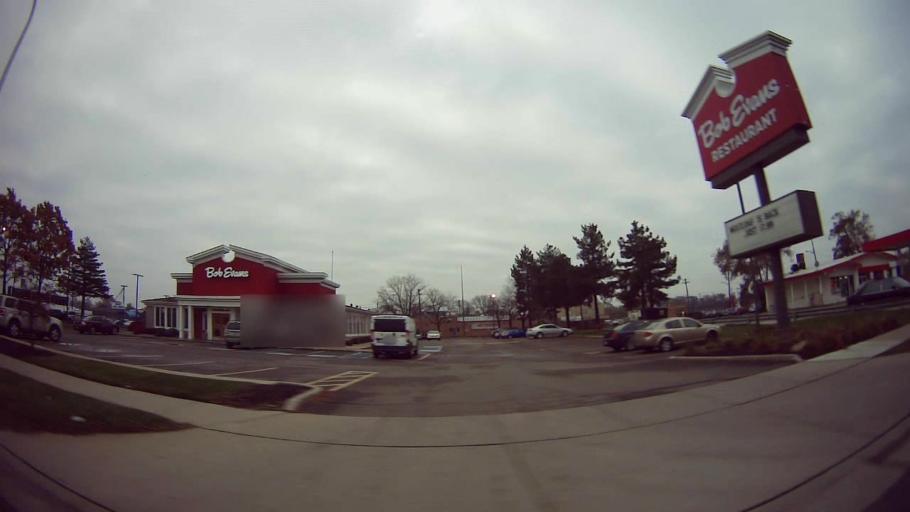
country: US
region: Michigan
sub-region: Wayne County
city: Dearborn Heights
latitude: 42.3006
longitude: -83.2678
